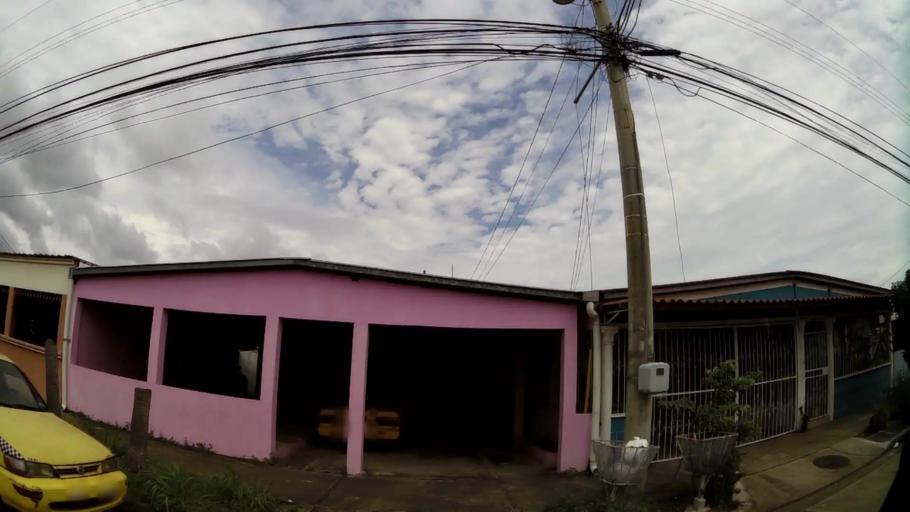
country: PA
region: Panama
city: Tocumen
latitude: 9.0450
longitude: -79.4118
